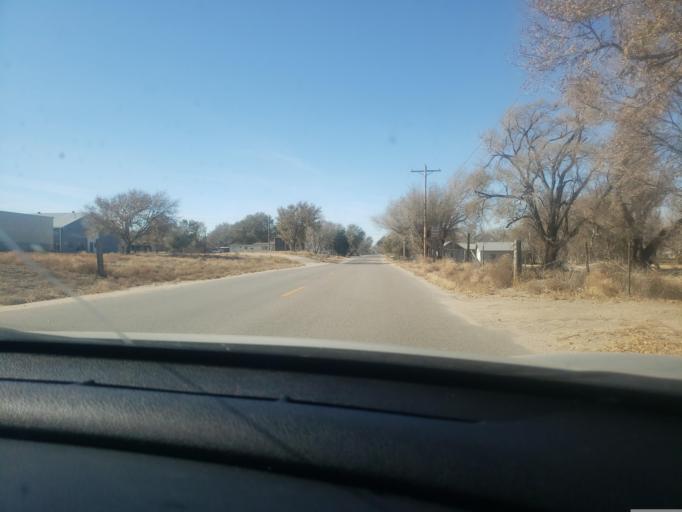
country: US
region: Kansas
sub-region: Finney County
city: Garden City
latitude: 37.9512
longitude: -100.8663
